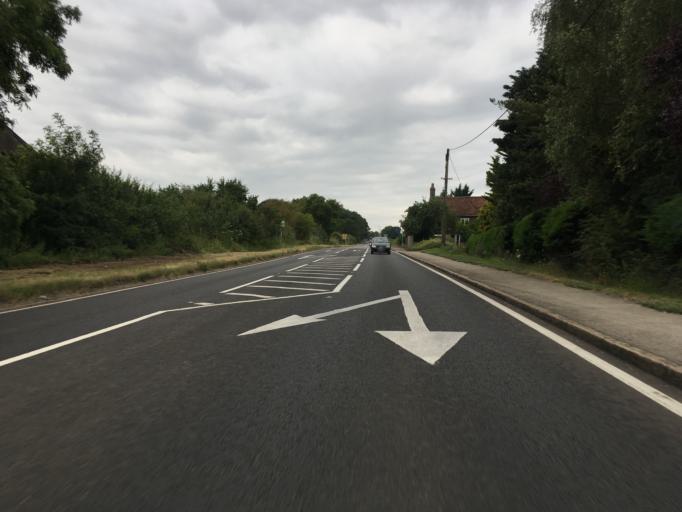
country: GB
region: England
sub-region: Central Bedfordshire
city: Kensworth
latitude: 51.8655
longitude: -0.4876
